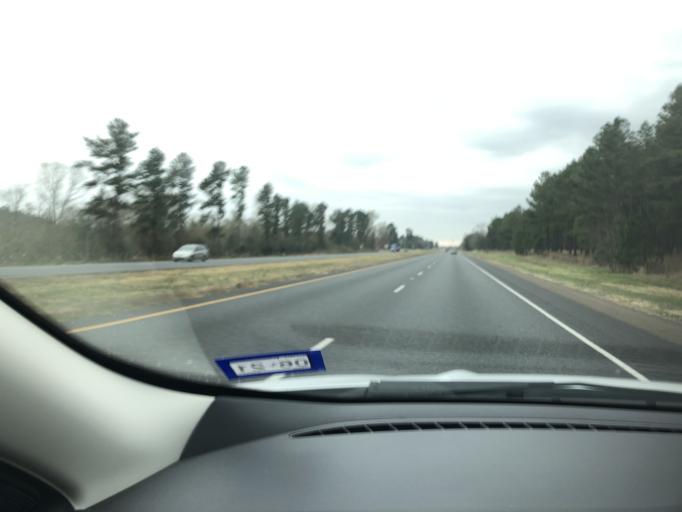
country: US
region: Texas
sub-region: Angelina County
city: Redland
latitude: 31.5036
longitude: -94.7061
